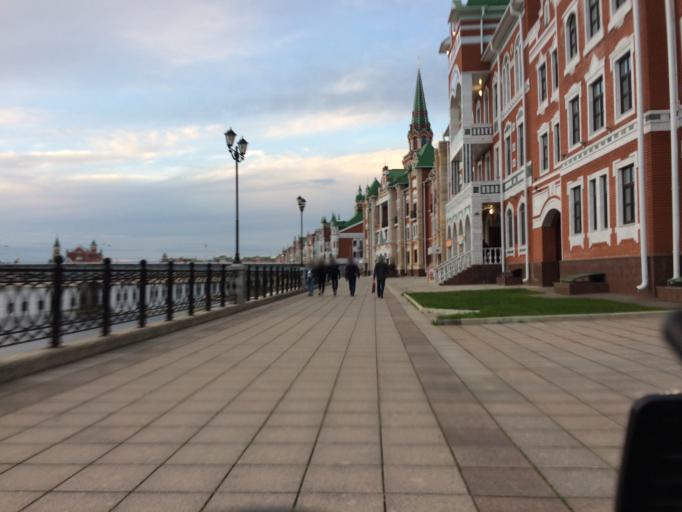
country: RU
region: Mariy-El
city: Yoshkar-Ola
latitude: 56.6314
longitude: 47.9074
